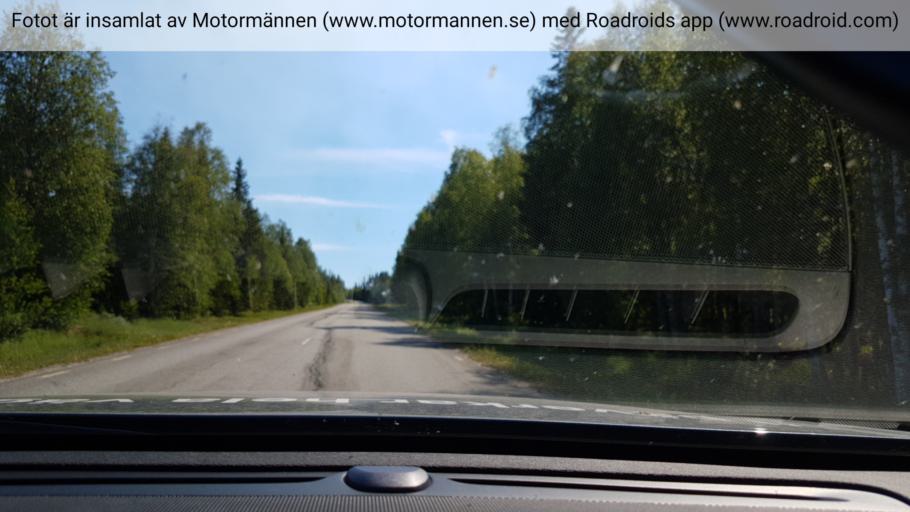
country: SE
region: Vaesterbotten
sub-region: Lycksele Kommun
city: Soderfors
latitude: 64.6665
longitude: 17.8379
